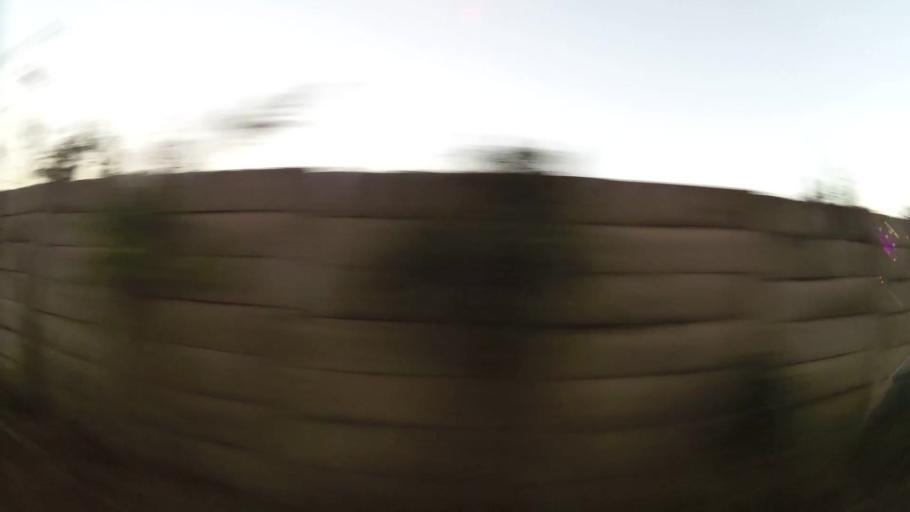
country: ZA
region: Gauteng
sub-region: City of Tshwane Metropolitan Municipality
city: Centurion
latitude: -25.8460
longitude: 28.1201
